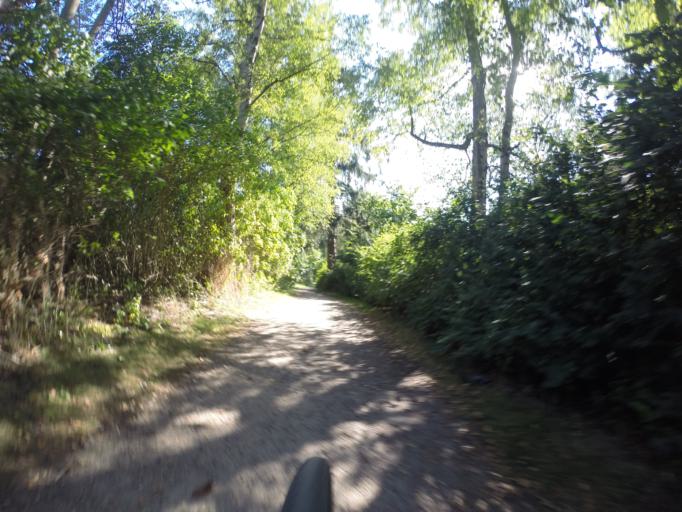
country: DK
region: Capital Region
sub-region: Herlev Kommune
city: Herlev
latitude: 55.7559
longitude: 12.4322
